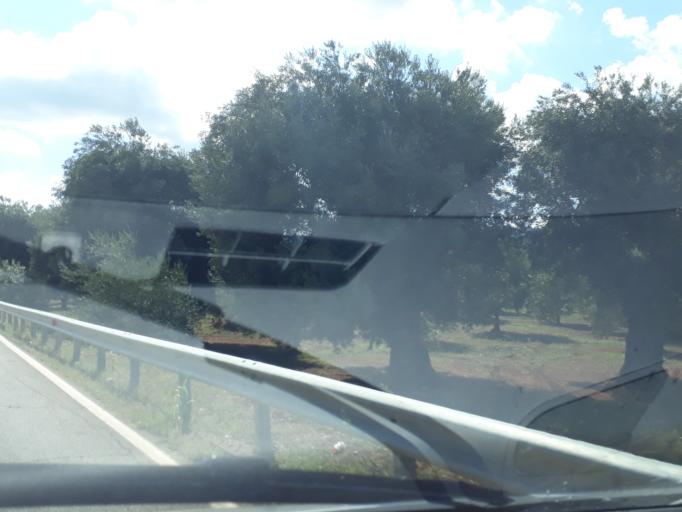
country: IT
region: Apulia
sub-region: Provincia di Brindisi
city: Fasano
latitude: 40.8203
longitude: 17.3768
